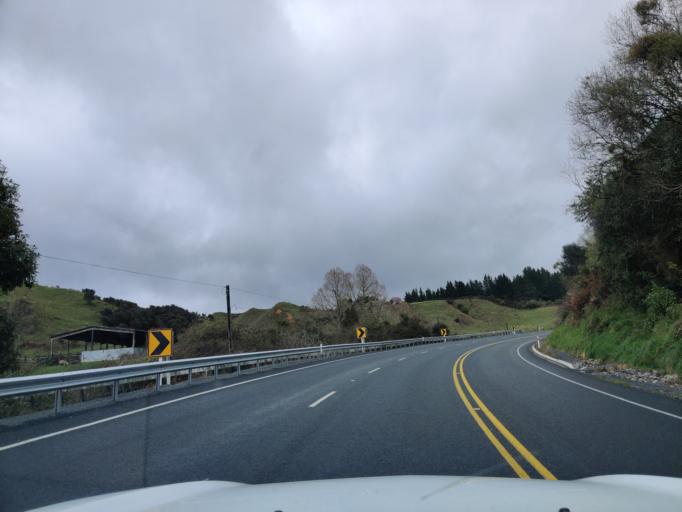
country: NZ
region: Waikato
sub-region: Otorohanga District
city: Otorohanga
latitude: -38.6344
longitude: 175.2086
